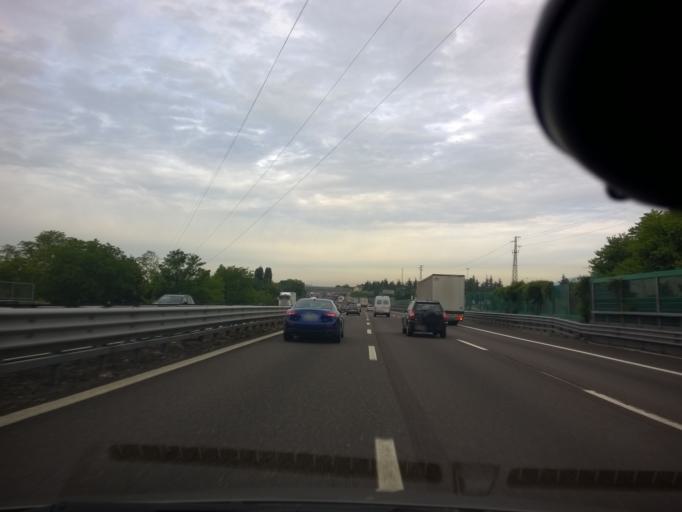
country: IT
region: Lombardy
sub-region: Provincia di Brescia
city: Lonato
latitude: 45.4535
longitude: 10.4830
